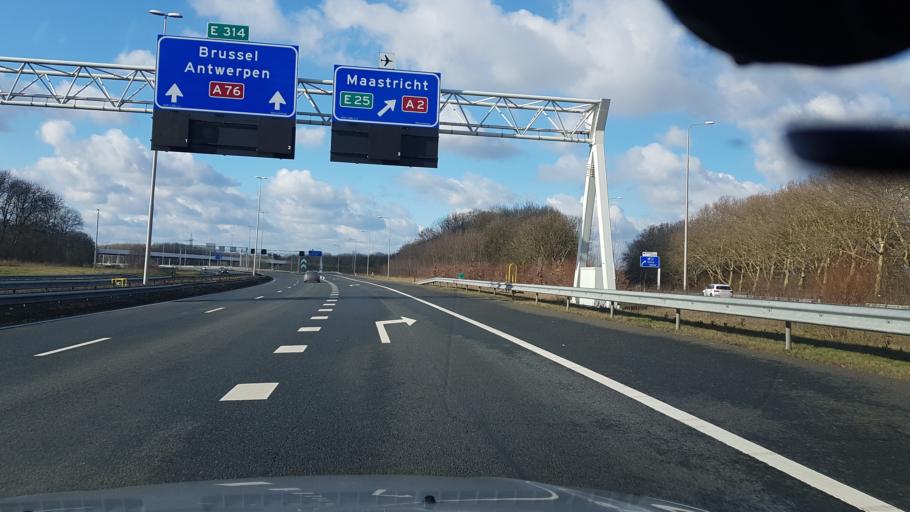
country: NL
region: Limburg
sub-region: Gemeente Beek
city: Beek
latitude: 50.9661
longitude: 5.7936
